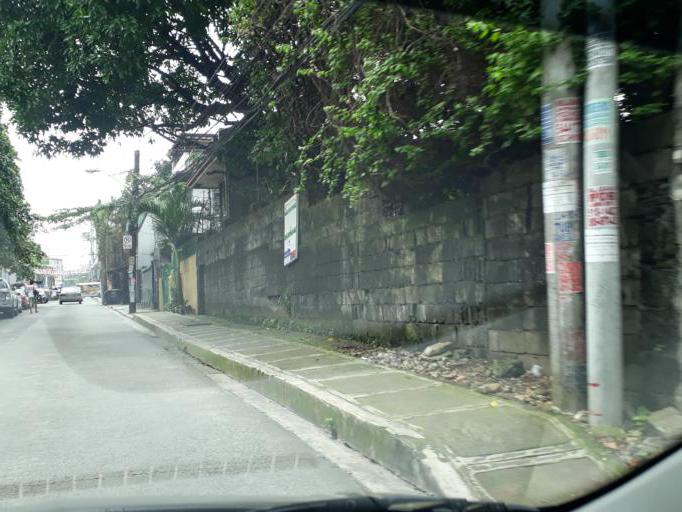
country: PH
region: Metro Manila
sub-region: Quezon City
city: Quezon City
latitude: 14.6279
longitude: 121.0565
